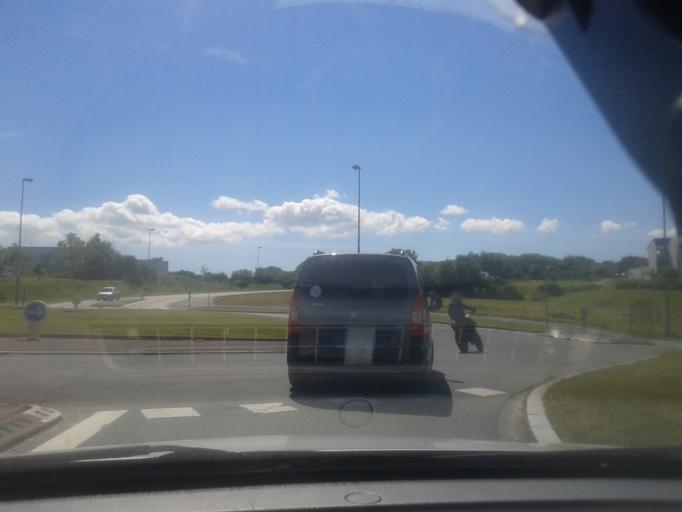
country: FR
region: Lower Normandy
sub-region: Departement de la Manche
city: Equeurdreville-Hainneville
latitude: 49.6357
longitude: -1.6529
